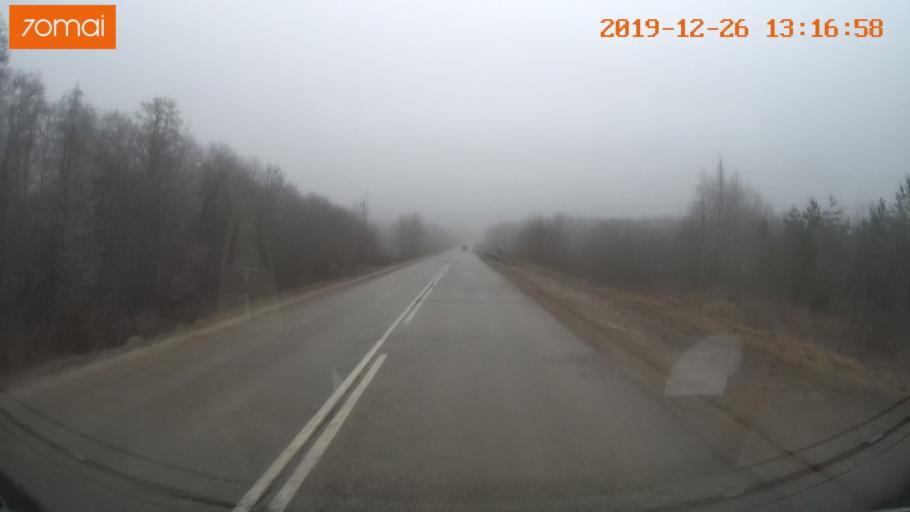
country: RU
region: Vologda
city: Cherepovets
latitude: 58.9754
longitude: 38.1110
